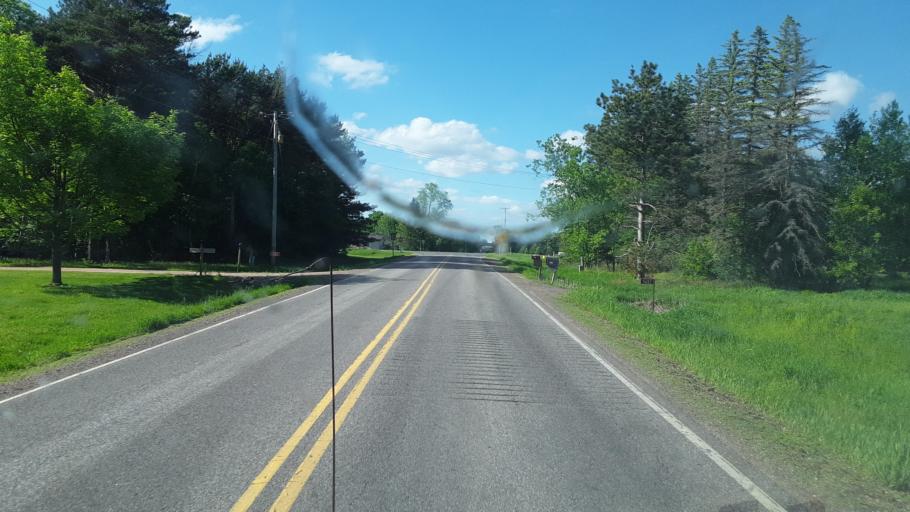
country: US
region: Wisconsin
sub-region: Wood County
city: Marshfield
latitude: 44.4521
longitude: -90.1611
